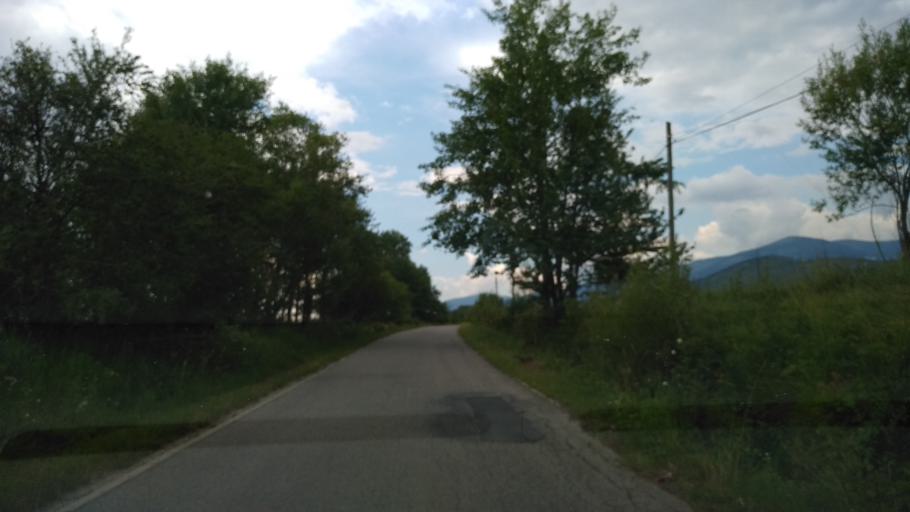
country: RO
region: Hunedoara
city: Salasu de Sus
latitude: 45.5054
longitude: 22.9600
